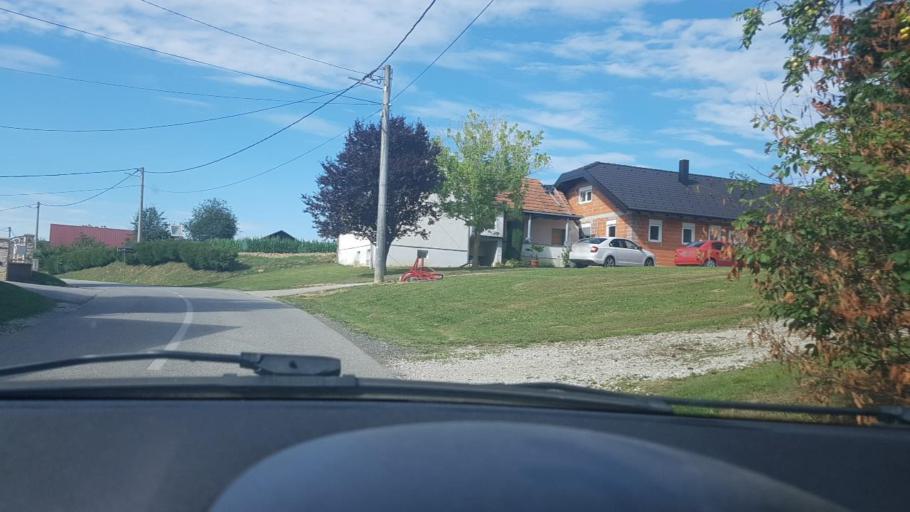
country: HR
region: Varazdinska
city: Tuzno
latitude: 46.2564
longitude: 16.1785
